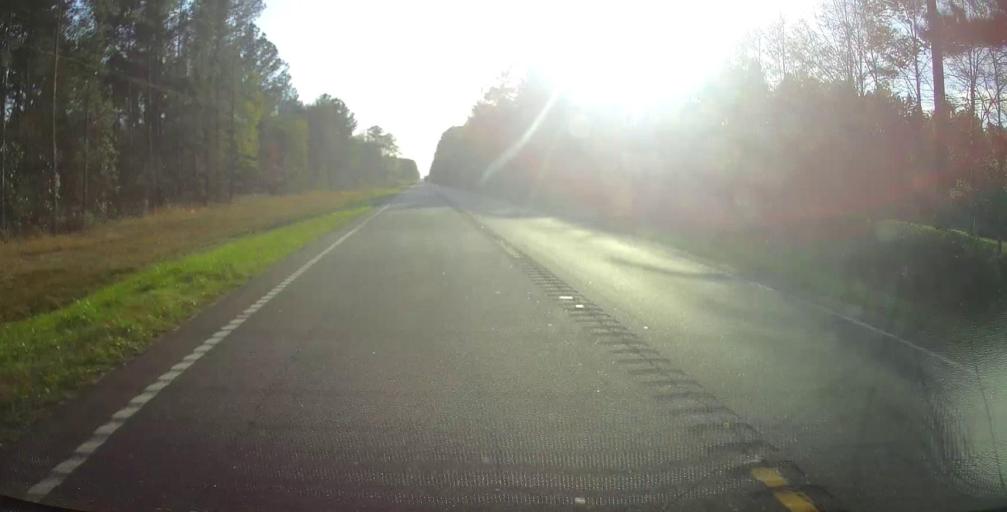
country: US
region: Georgia
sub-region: Tattnall County
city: Reidsville
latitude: 32.1402
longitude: -82.0341
